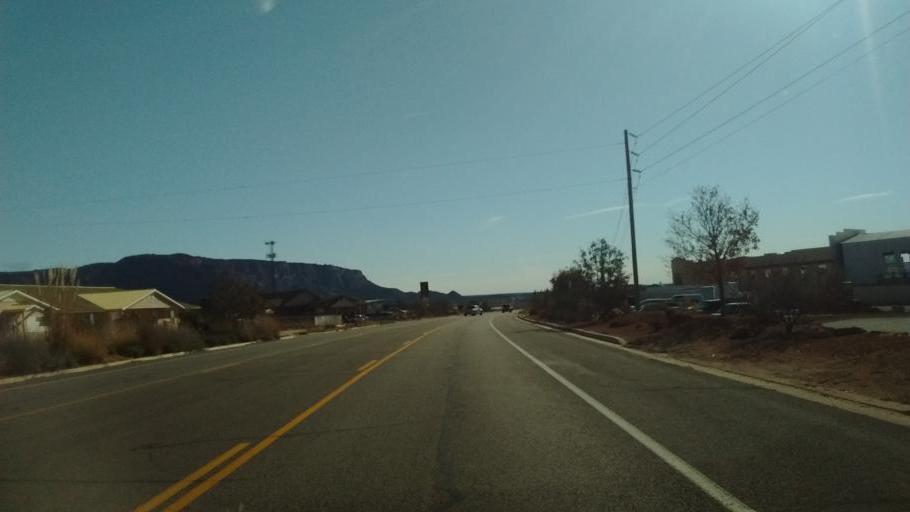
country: US
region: Arizona
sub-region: Mohave County
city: Colorado City
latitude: 37.0029
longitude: -113.0014
